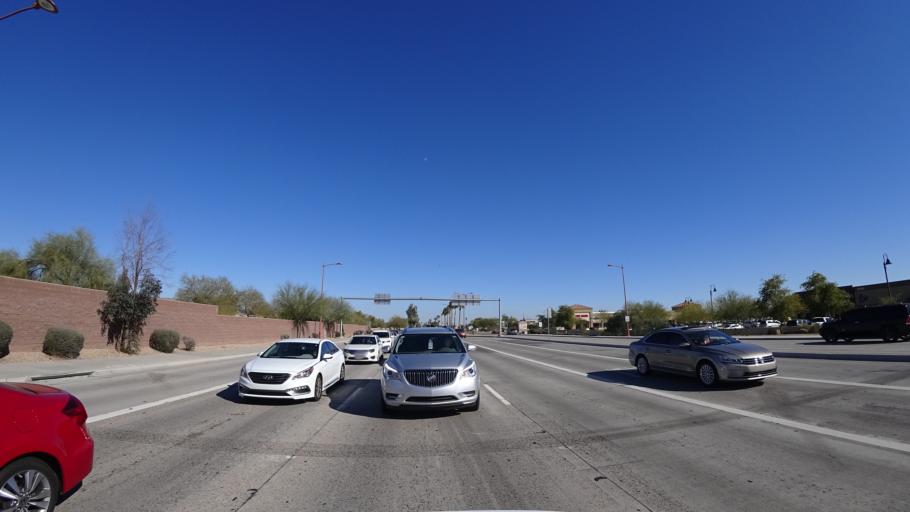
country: US
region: Arizona
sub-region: Maricopa County
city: Sun City West
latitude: 33.6389
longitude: -112.4171
